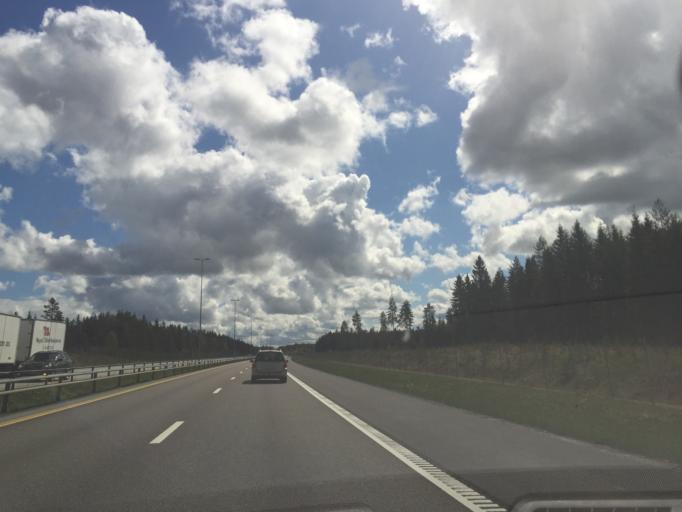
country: NO
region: Akershus
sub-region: Ullensaker
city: Jessheim
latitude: 60.2076
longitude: 11.1864
